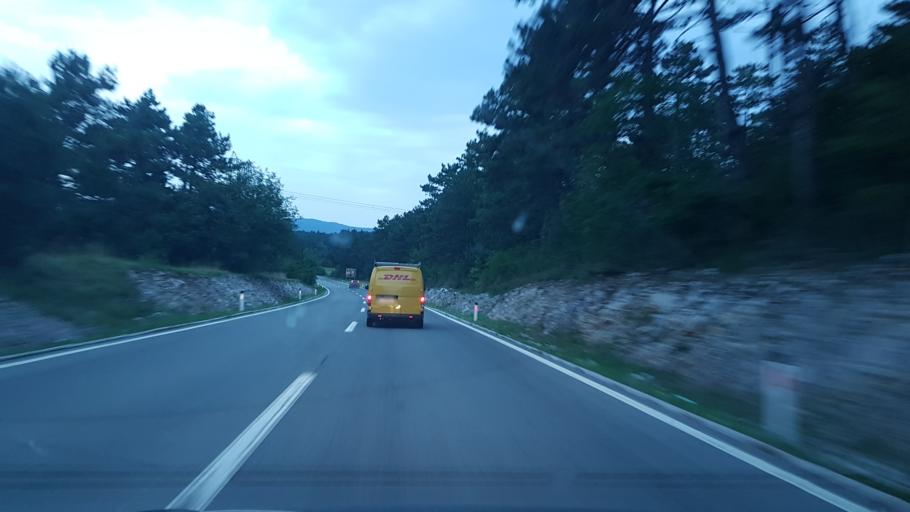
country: SI
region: Divaca
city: Divaca
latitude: 45.6930
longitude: 13.9837
